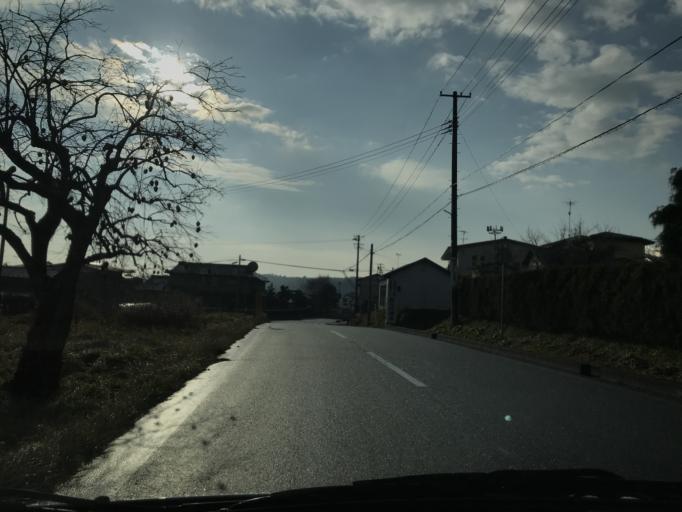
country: JP
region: Iwate
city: Ichinoseki
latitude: 38.8494
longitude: 141.1606
